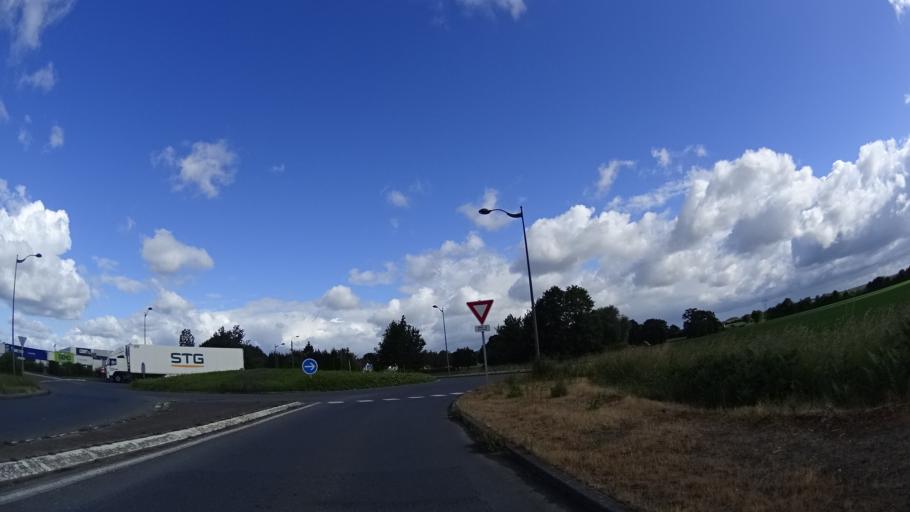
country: FR
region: Brittany
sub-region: Departement d'Ille-et-Vilaine
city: Hede-Bazouges
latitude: 48.3020
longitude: -1.8163
